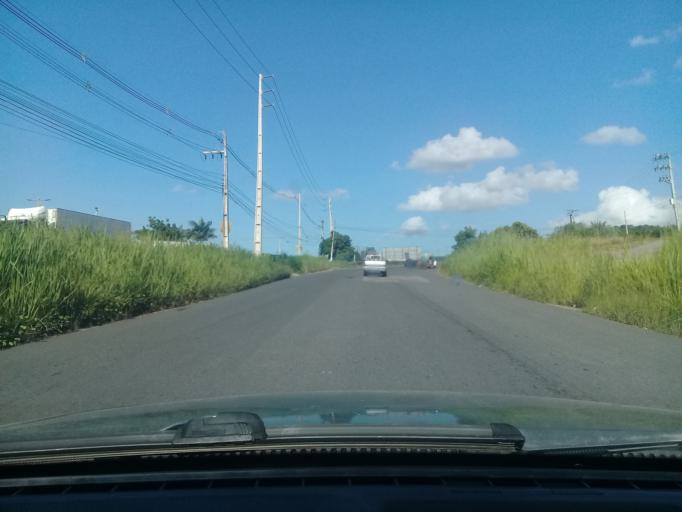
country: BR
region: Pernambuco
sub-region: Vitoria De Santo Antao
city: Vitoria de Santo Antao
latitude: -8.1168
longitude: -35.2644
